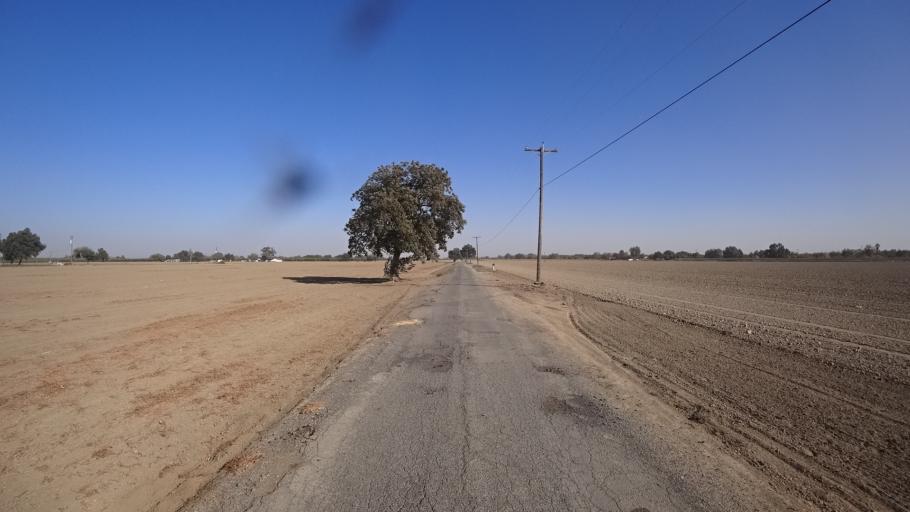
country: US
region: California
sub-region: Yolo County
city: Woodland
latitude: 38.7359
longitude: -121.8025
